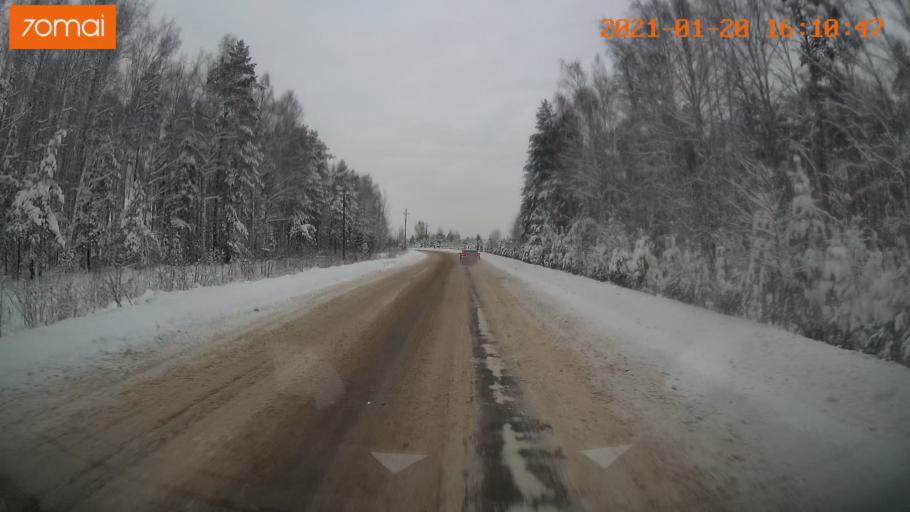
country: RU
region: Vladimir
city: Sudogda
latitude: 56.0955
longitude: 40.7858
